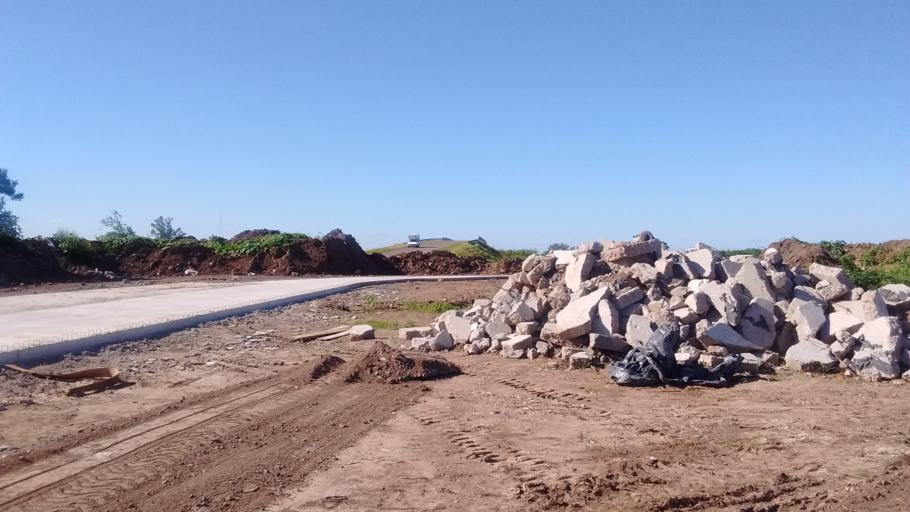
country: AR
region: Santa Fe
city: Perez
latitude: -32.9474
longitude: -60.7384
